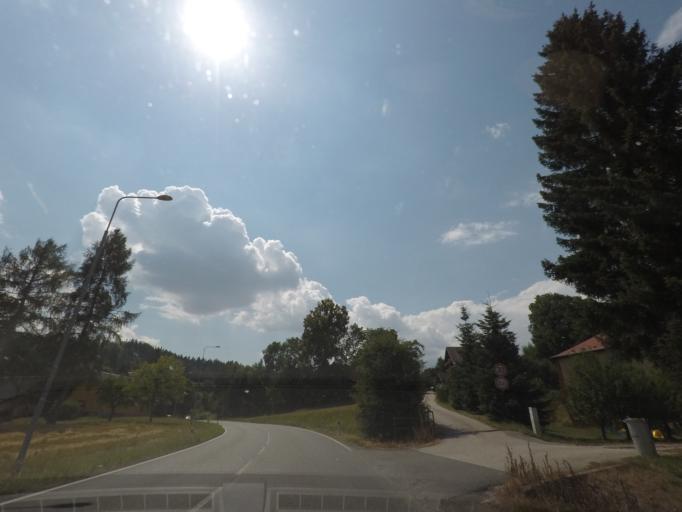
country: CZ
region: Kralovehradecky
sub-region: Okres Jicin
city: Pecka
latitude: 50.5332
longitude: 15.6187
